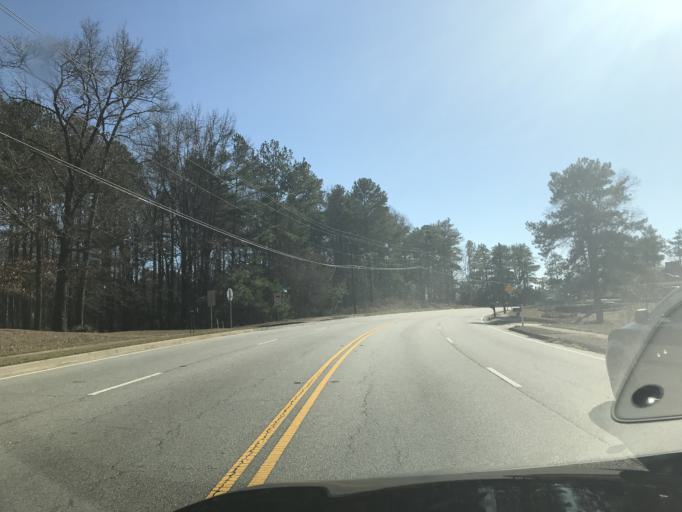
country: US
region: Georgia
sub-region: Cobb County
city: Mableton
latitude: 33.7838
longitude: -84.5741
